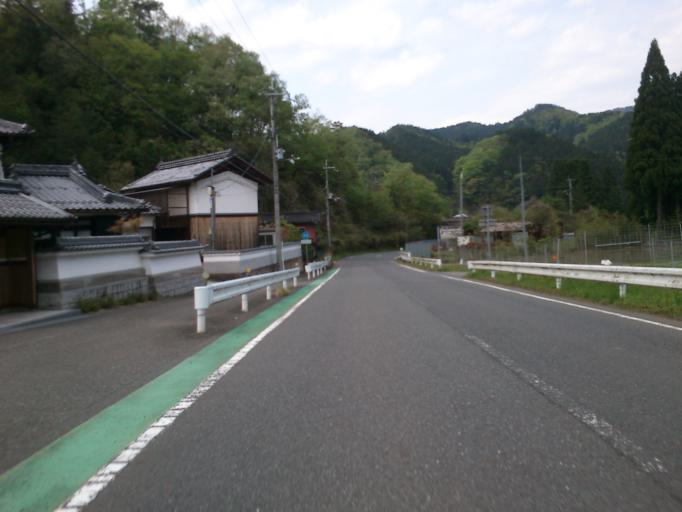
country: JP
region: Kyoto
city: Fukuchiyama
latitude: 35.3221
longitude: 134.9577
